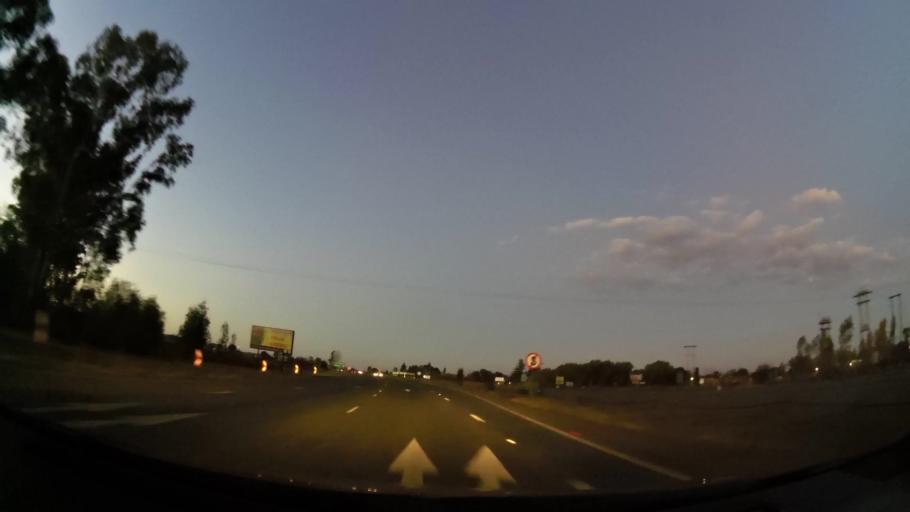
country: ZA
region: North-West
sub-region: Dr Kenneth Kaunda District Municipality
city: Potchefstroom
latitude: -26.7051
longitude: 27.1241
